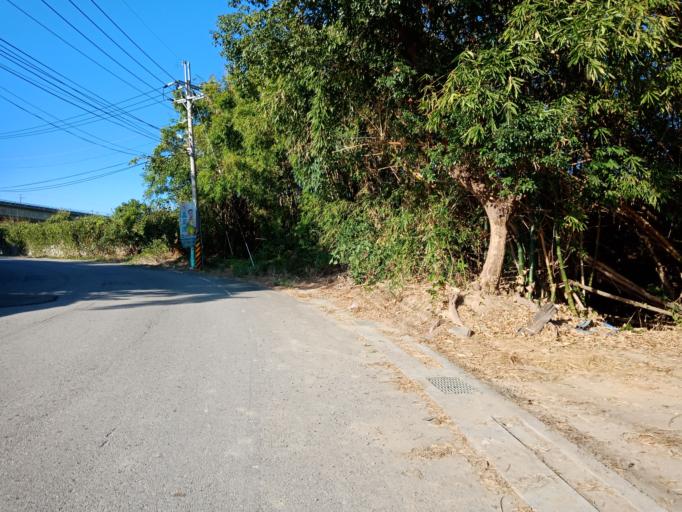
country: TW
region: Taiwan
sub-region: Miaoli
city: Miaoli
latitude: 24.4846
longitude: 120.7032
